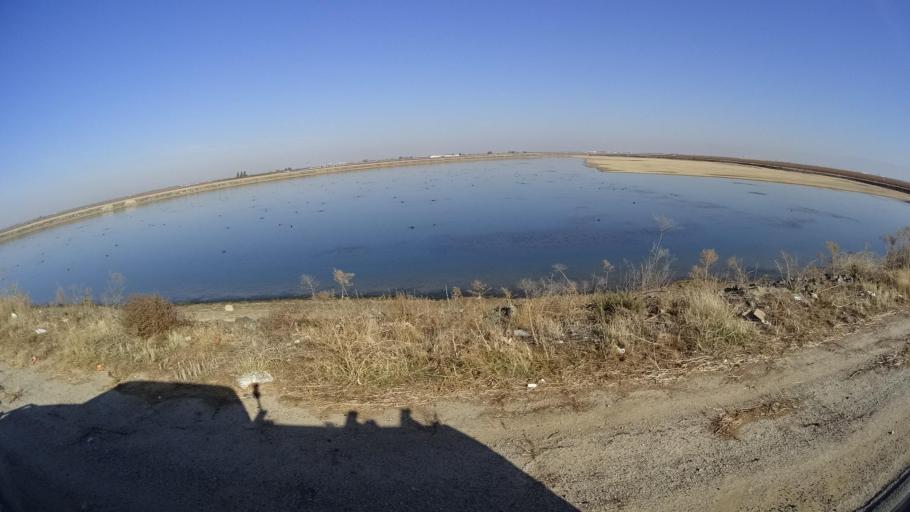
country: US
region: California
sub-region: Kern County
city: Delano
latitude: 35.7470
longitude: -119.1792
